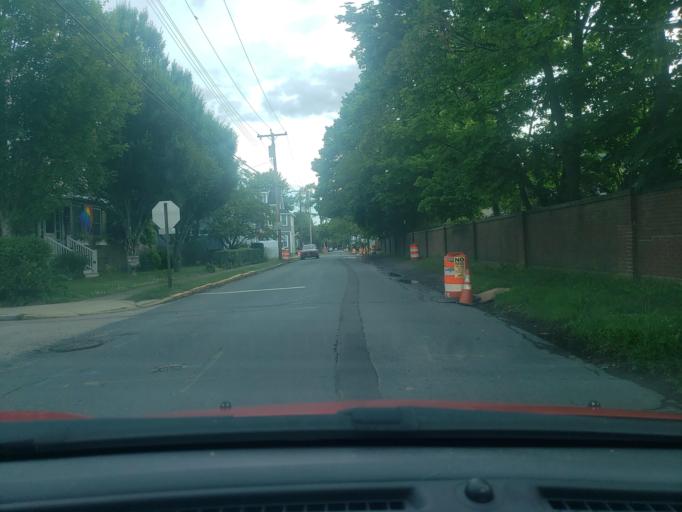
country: US
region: Rhode Island
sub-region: Newport County
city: Newport
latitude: 41.4803
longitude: -71.3022
